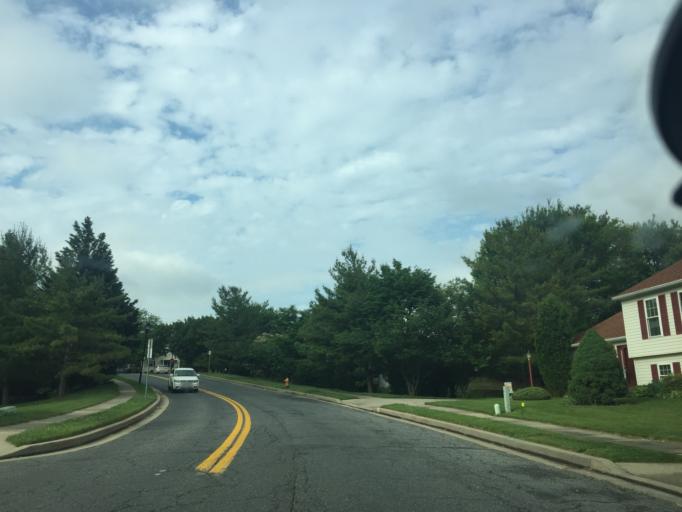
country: US
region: Maryland
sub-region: Baltimore County
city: Carney
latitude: 39.3938
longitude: -76.4970
